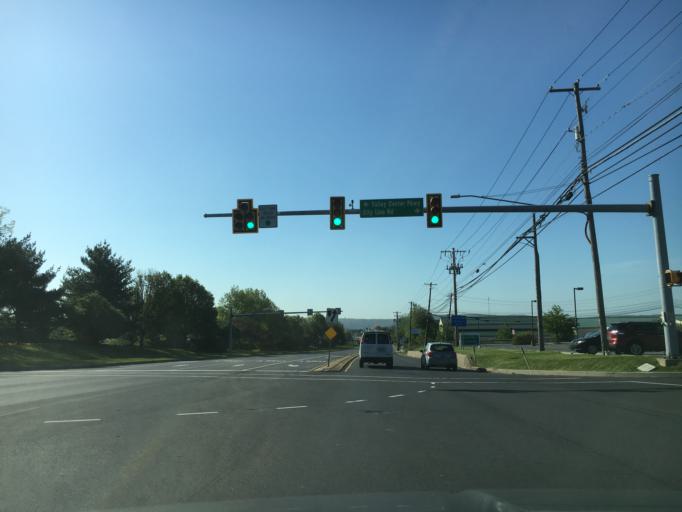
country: US
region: Pennsylvania
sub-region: Northampton County
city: Bethlehem
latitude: 40.6557
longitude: -75.4165
